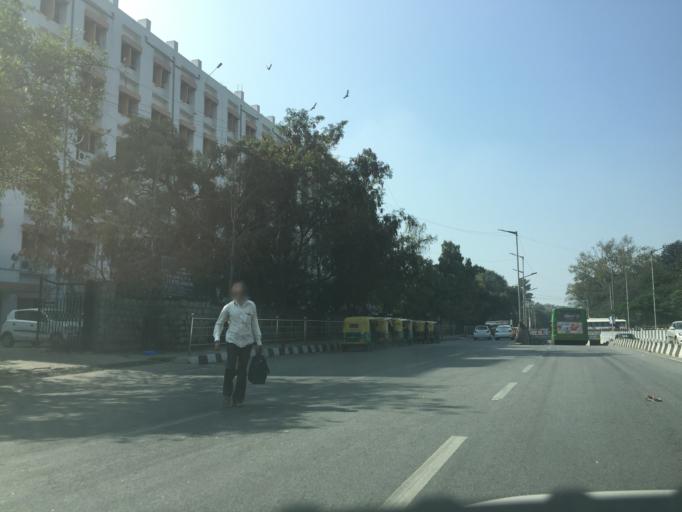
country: IN
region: Karnataka
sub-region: Bangalore Urban
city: Bangalore
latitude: 12.9791
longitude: 77.5851
